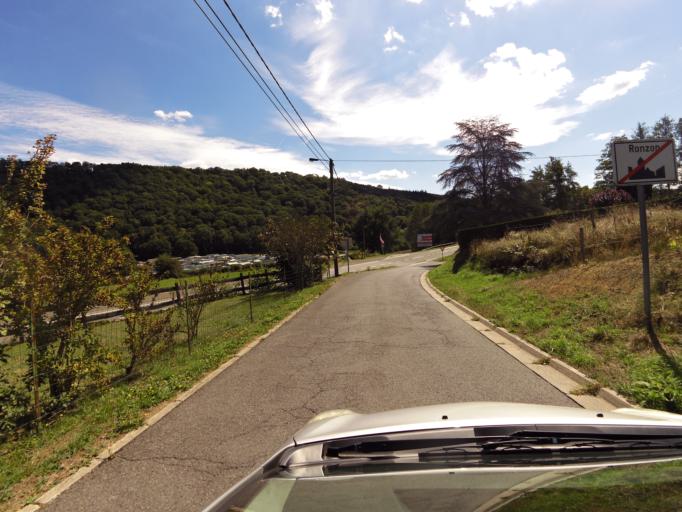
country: BE
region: Wallonia
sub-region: Province du Luxembourg
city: Rendeux
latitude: 50.2251
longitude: 5.5242
